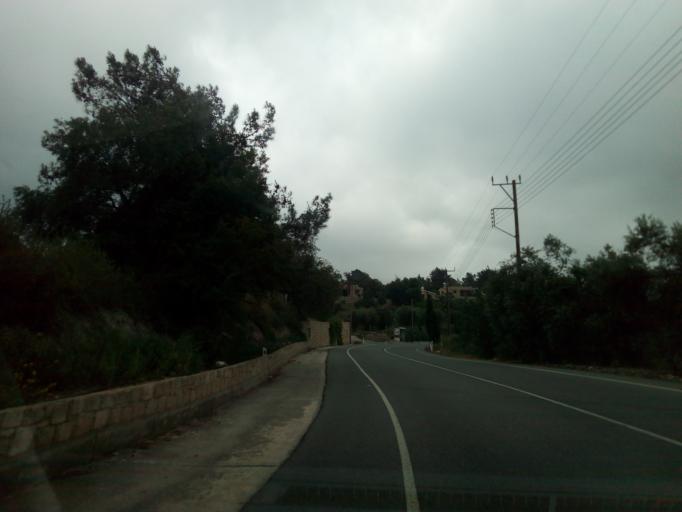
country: CY
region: Pafos
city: Mesogi
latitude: 34.9065
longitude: 32.5488
